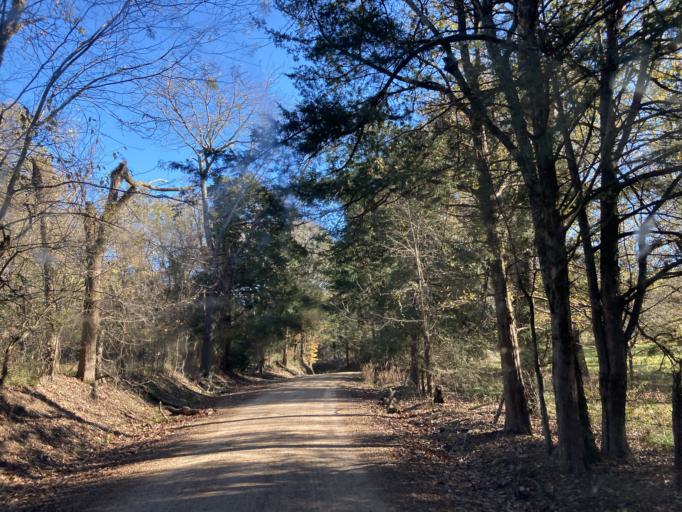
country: US
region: Mississippi
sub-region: Yazoo County
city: Yazoo City
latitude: 32.6966
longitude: -90.4948
